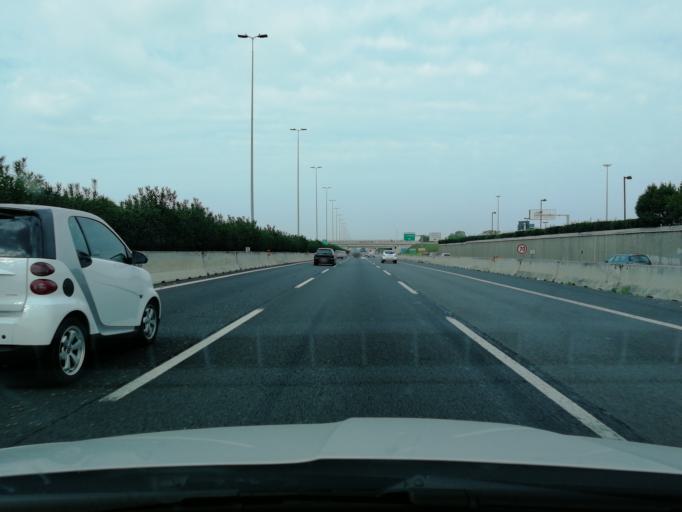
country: IT
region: Latium
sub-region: Citta metropolitana di Roma Capitale
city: Ciampino
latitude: 41.8499
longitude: 12.5965
